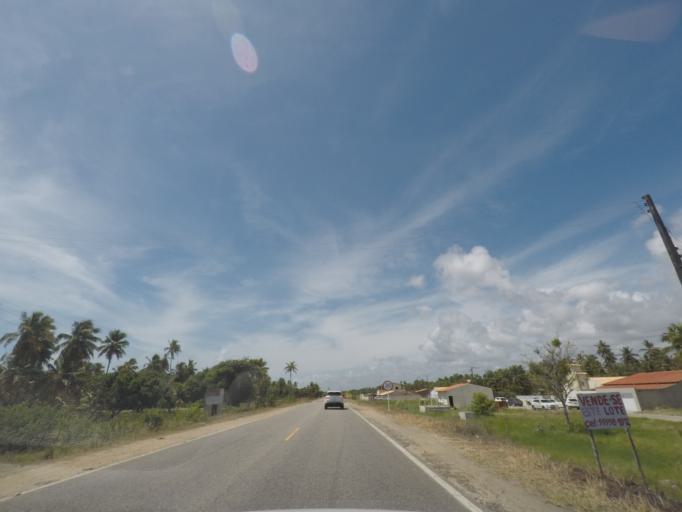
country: BR
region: Sergipe
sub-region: Sao Cristovao
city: Sao Cristovao
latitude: -11.2176
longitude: -37.2208
